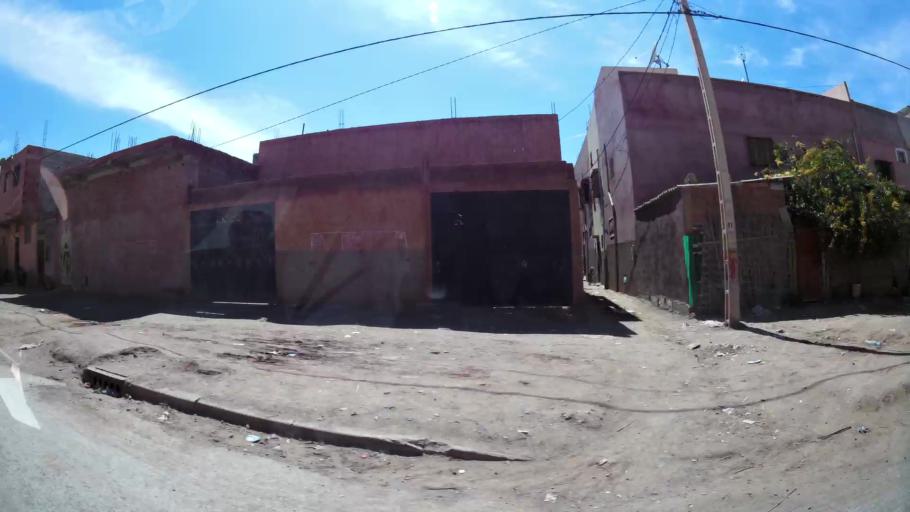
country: MA
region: Marrakech-Tensift-Al Haouz
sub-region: Marrakech
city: Marrakesh
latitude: 31.6364
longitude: -8.0820
